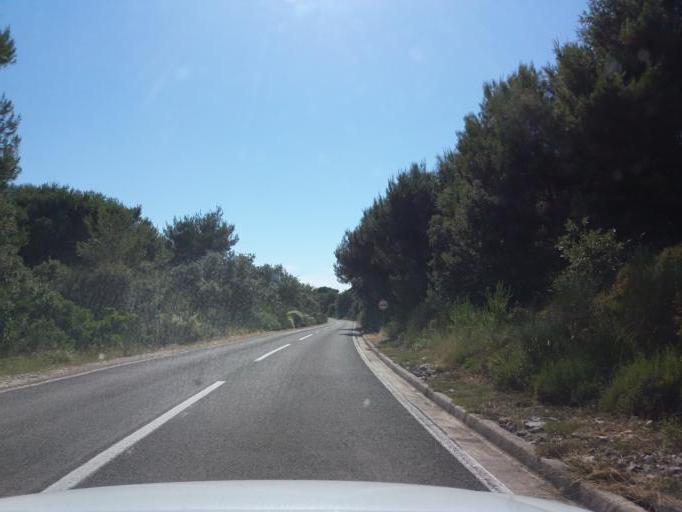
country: HR
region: Zadarska
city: Ugljan
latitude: 44.1360
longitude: 14.8699
